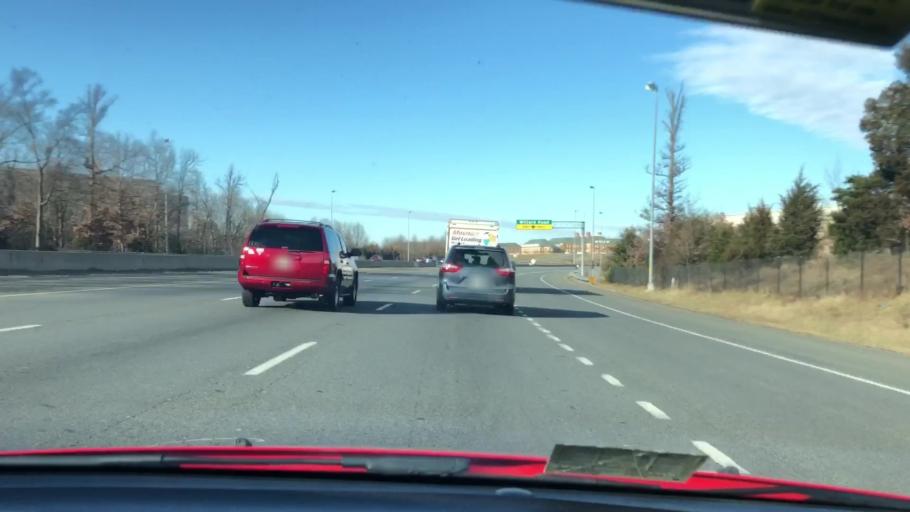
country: US
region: Virginia
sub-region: Fairfax County
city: Chantilly
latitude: 38.8809
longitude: -77.4490
